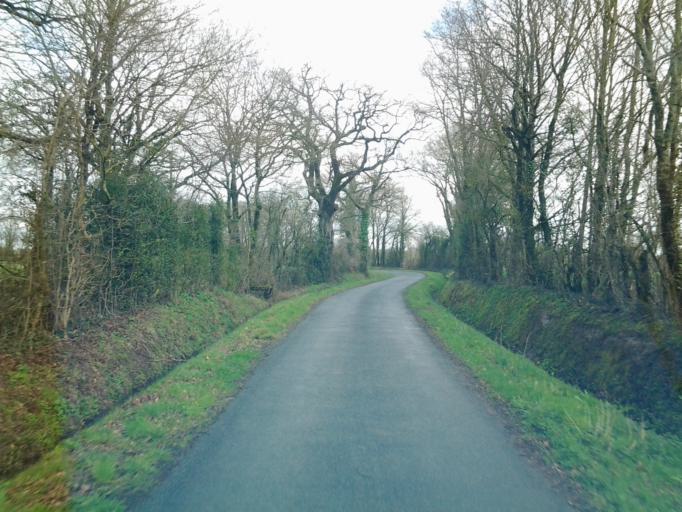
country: FR
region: Pays de la Loire
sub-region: Departement de la Vendee
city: La Chaize-le-Vicomte
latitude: 46.6584
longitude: -1.3499
